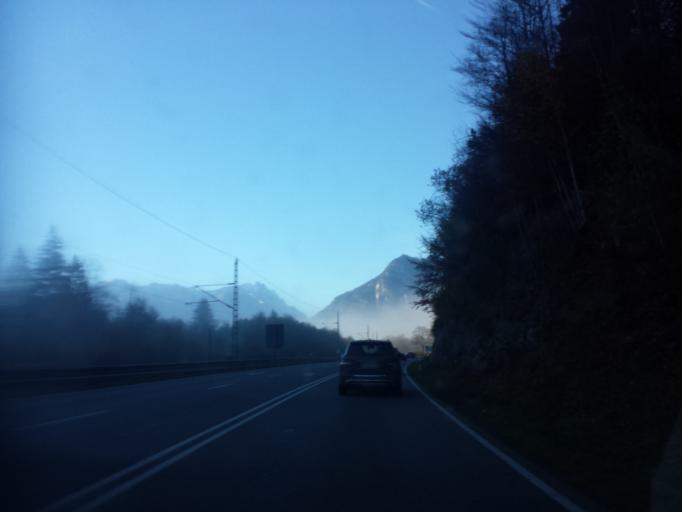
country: DE
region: Bavaria
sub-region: Upper Bavaria
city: Oberau
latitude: 47.5533
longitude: 11.1344
